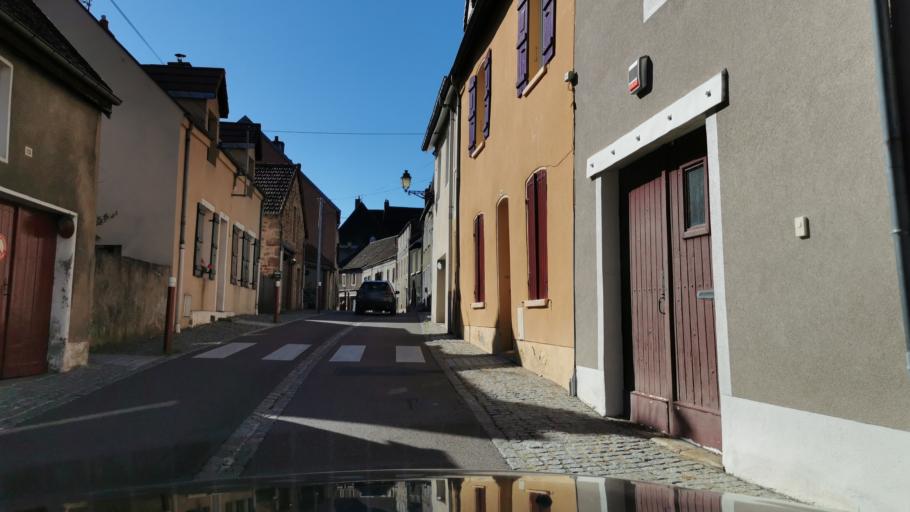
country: FR
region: Bourgogne
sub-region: Departement de Saone-et-Loire
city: Montcenis
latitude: 46.7887
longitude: 4.3901
